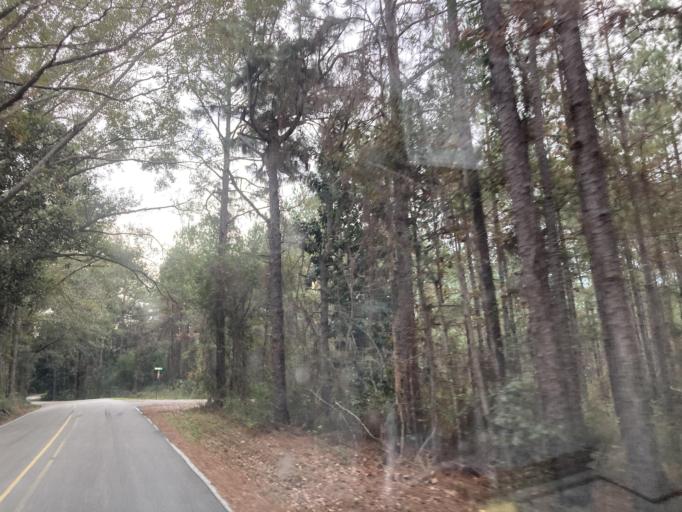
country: US
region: Mississippi
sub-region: Lamar County
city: Purvis
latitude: 31.1745
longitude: -89.3899
